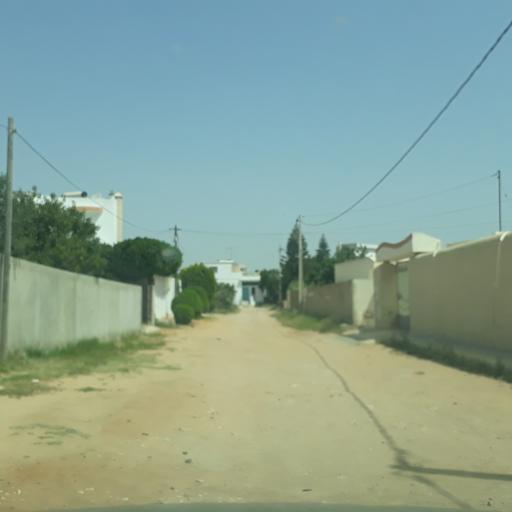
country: TN
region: Safaqis
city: Al Qarmadah
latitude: 34.7971
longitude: 10.7628
